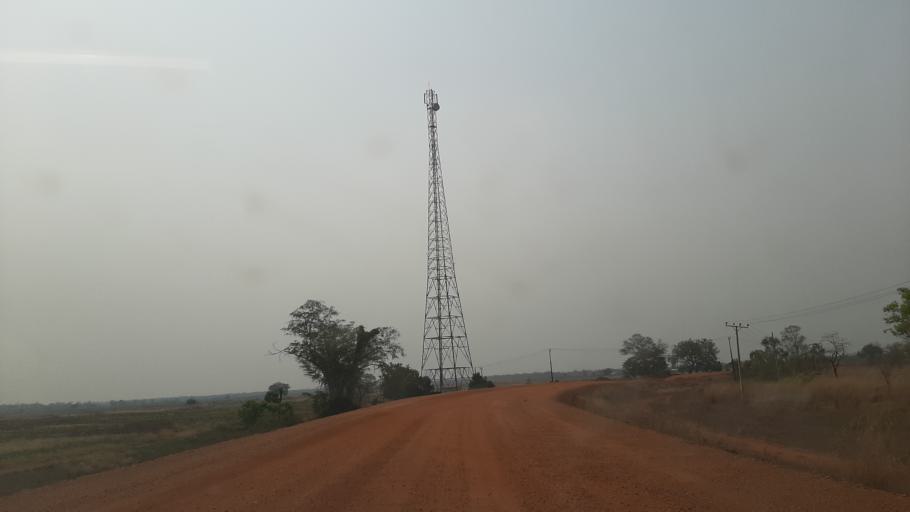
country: ET
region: Gambela
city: Gambela
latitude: 8.1561
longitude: 34.3378
